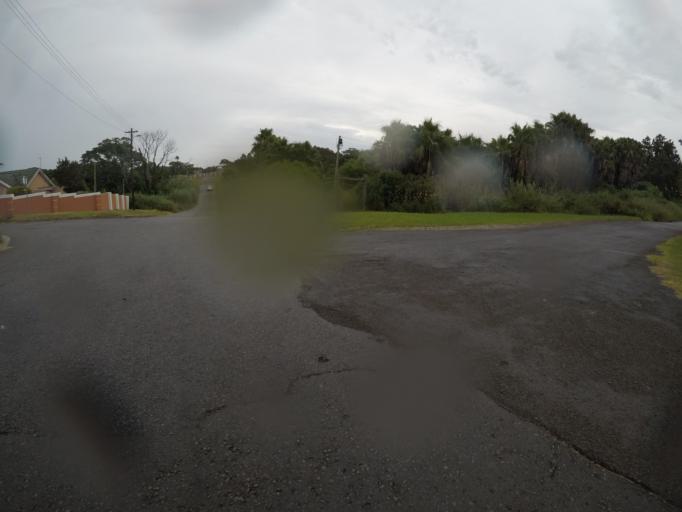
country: ZA
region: Eastern Cape
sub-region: Buffalo City Metropolitan Municipality
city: East London
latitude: -32.9877
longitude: 27.8598
